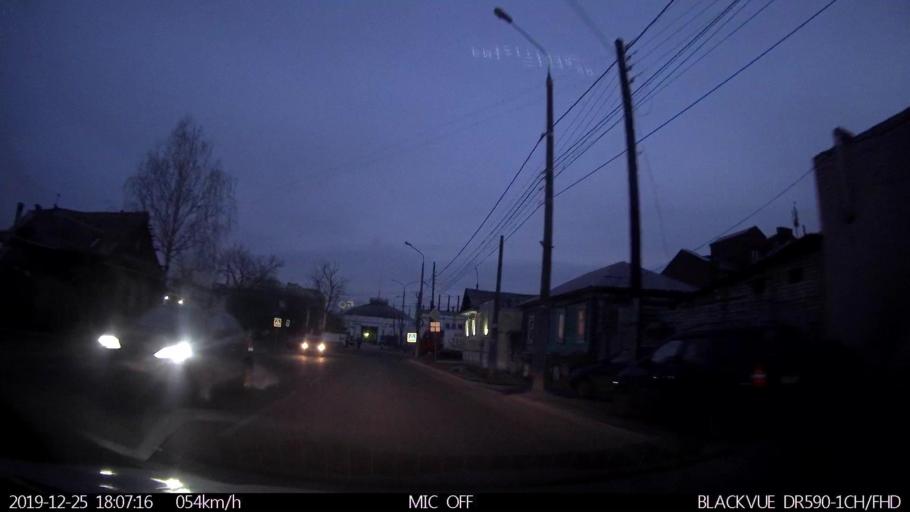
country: RU
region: Nizjnij Novgorod
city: Nizhniy Novgorod
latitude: 56.3159
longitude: 43.9521
